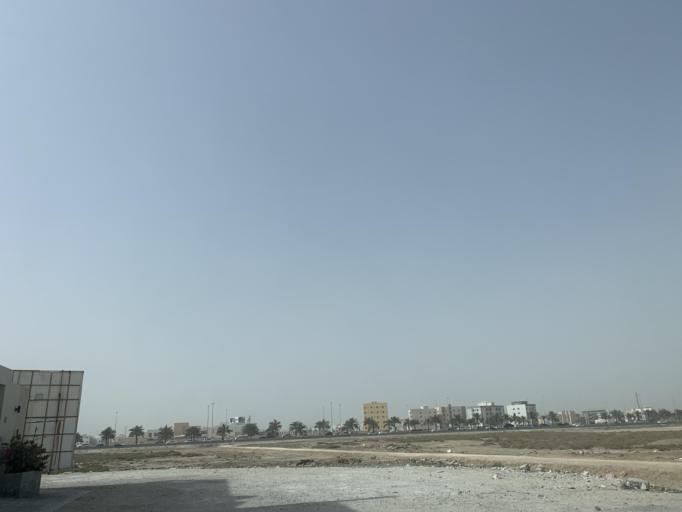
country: BH
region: Northern
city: Madinat `Isa
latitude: 26.1888
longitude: 50.5144
